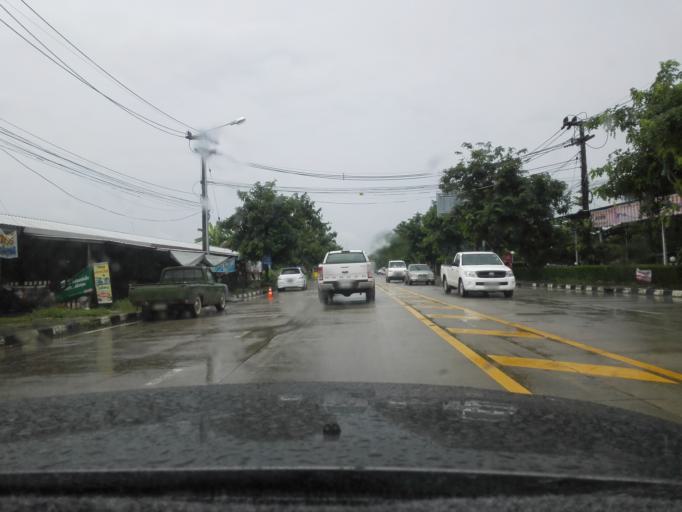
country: TH
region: Tak
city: Mae Sot
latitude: 16.7152
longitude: 98.5838
